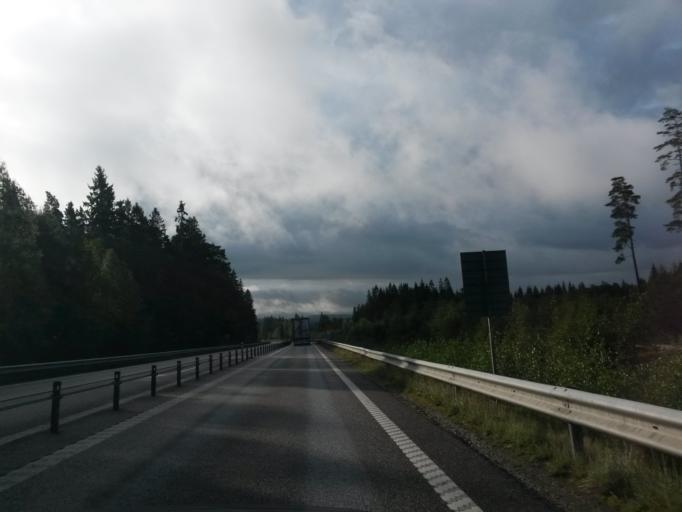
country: SE
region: Vaestra Goetaland
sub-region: Boras Kommun
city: Dalsjofors
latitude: 57.6333
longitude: 13.0836
